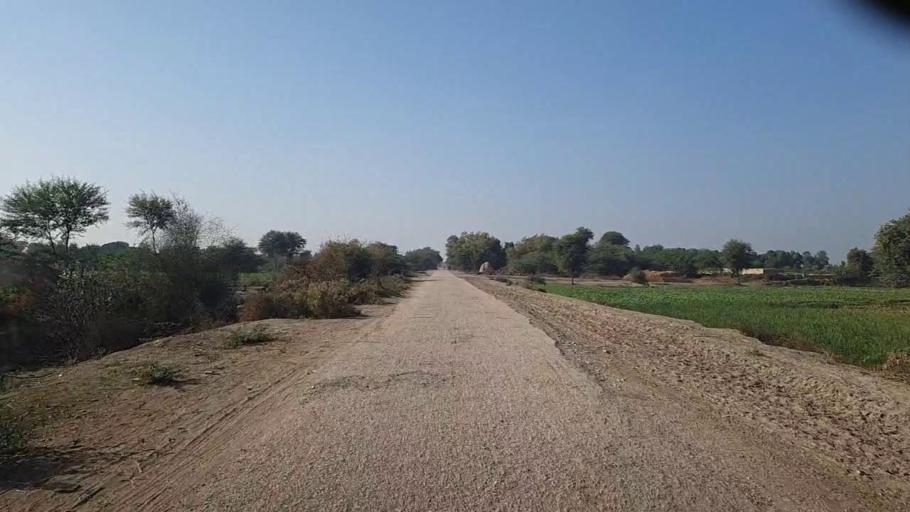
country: PK
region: Sindh
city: Darya Khan Marri
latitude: 26.6732
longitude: 68.3816
